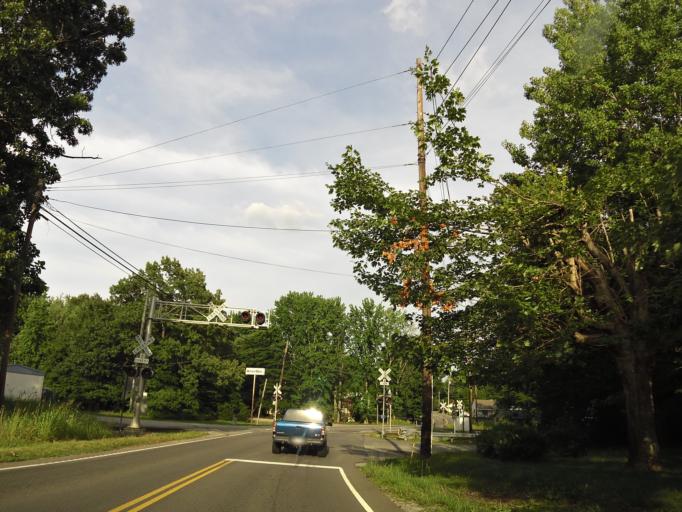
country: US
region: Tennessee
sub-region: Dickson County
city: Dickson
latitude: 36.0638
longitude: -87.3514
